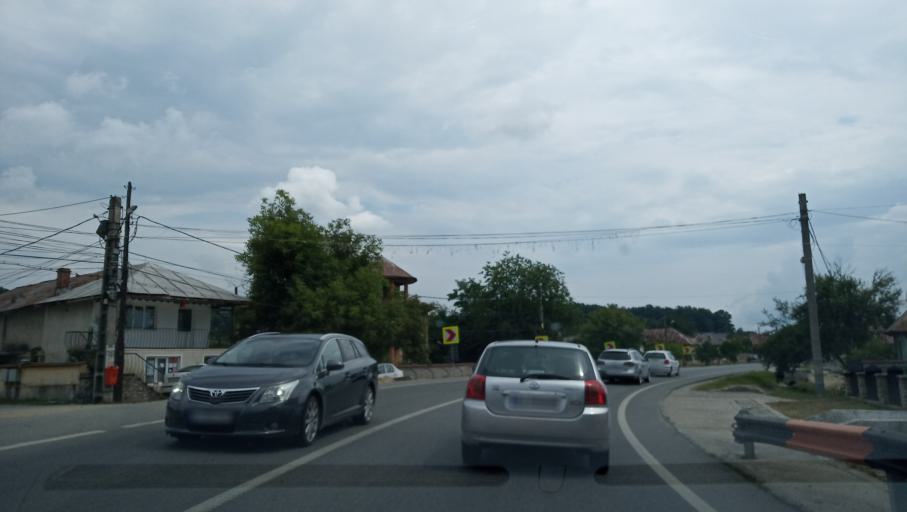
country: RO
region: Gorj
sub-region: Comuna Balteni
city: Pesteana Jiu
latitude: 44.8464
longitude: 23.3035
